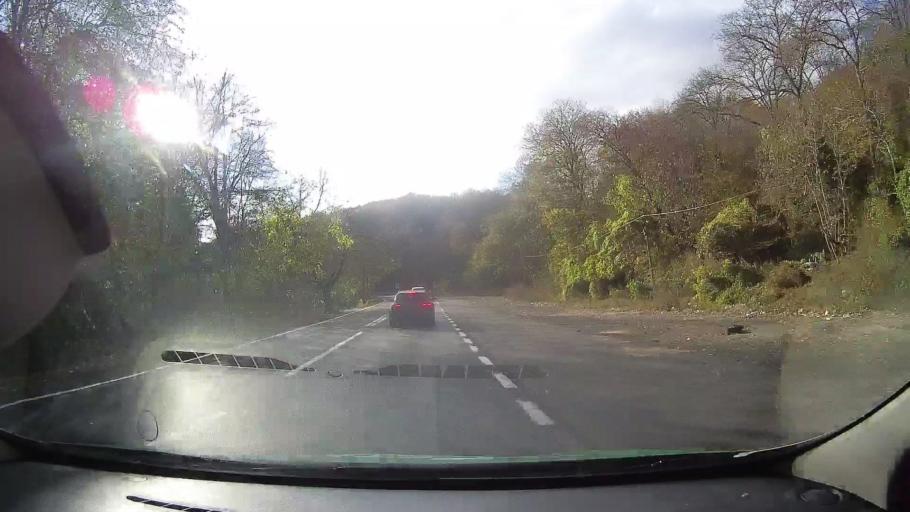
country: RO
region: Tulcea
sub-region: Comuna Ciucurova
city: Ciucurova
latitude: 44.9180
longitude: 28.4232
